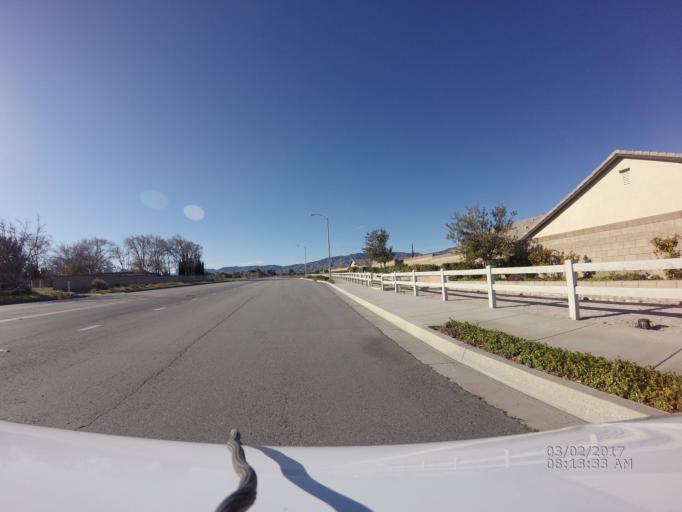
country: US
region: California
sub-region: Los Angeles County
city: Quartz Hill
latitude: 34.6396
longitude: -118.1833
